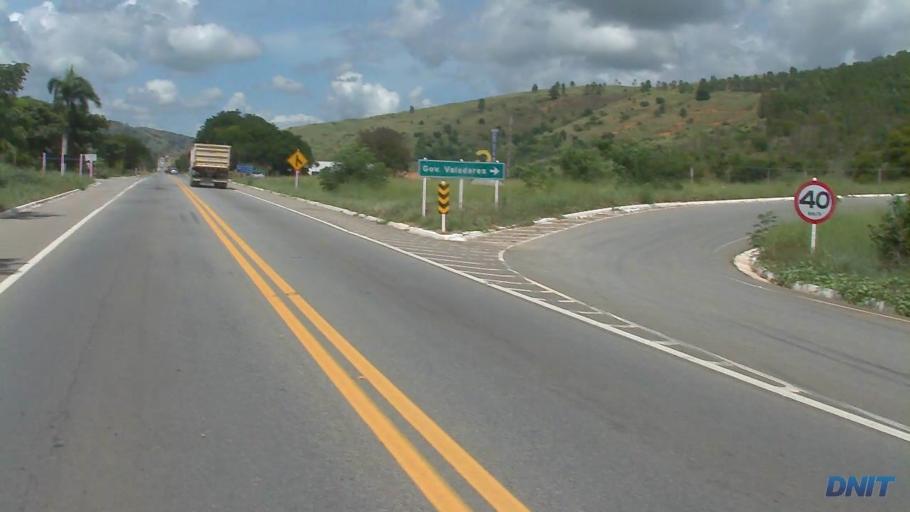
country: BR
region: Minas Gerais
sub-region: Governador Valadares
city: Governador Valadares
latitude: -18.9228
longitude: -42.0292
